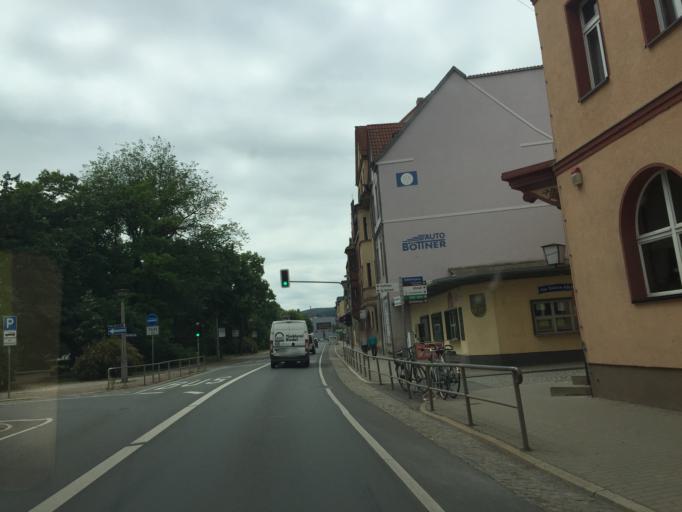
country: DE
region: Thuringia
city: Rudolstadt
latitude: 50.7191
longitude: 11.3396
